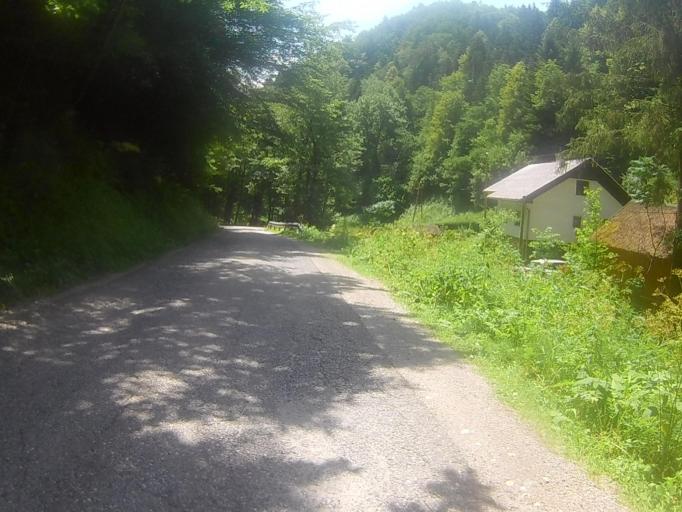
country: SI
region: Ruse
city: Bistrica ob Dravi
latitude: 46.5666
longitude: 15.5249
